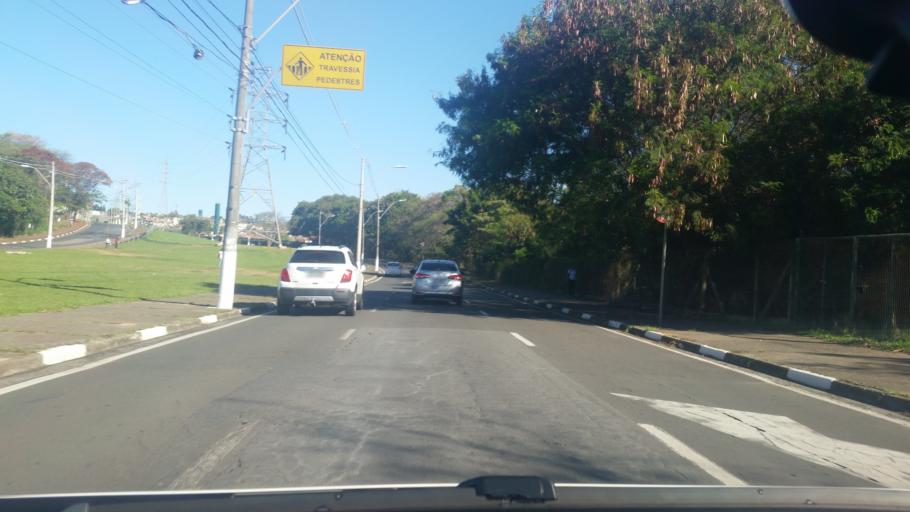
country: BR
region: Sao Paulo
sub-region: Campinas
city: Campinas
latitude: -22.8521
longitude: -47.0592
